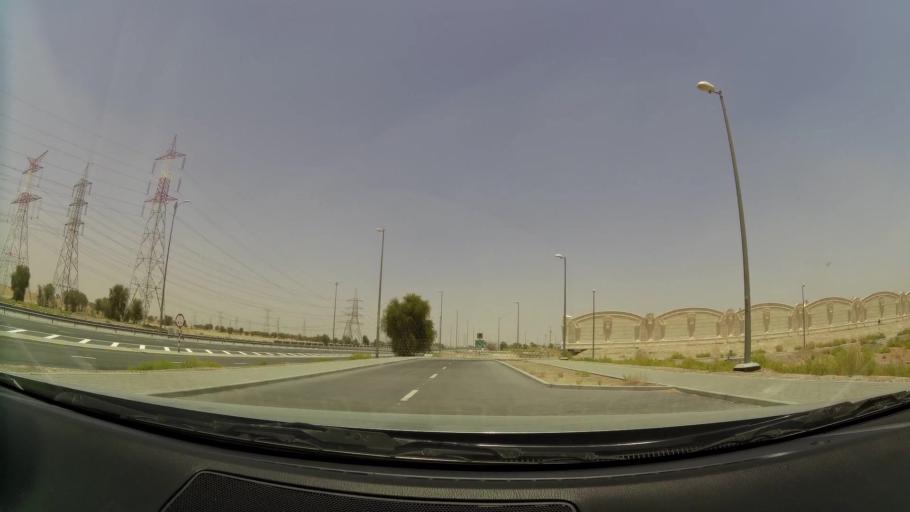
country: OM
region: Al Buraimi
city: Al Buraymi
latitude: 24.2731
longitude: 55.7141
